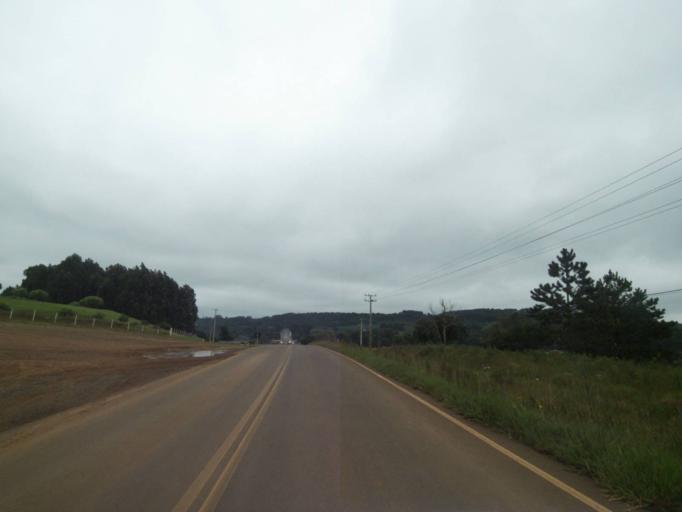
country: BR
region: Parana
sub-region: Pitanga
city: Pitanga
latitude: -24.9315
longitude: -51.8760
